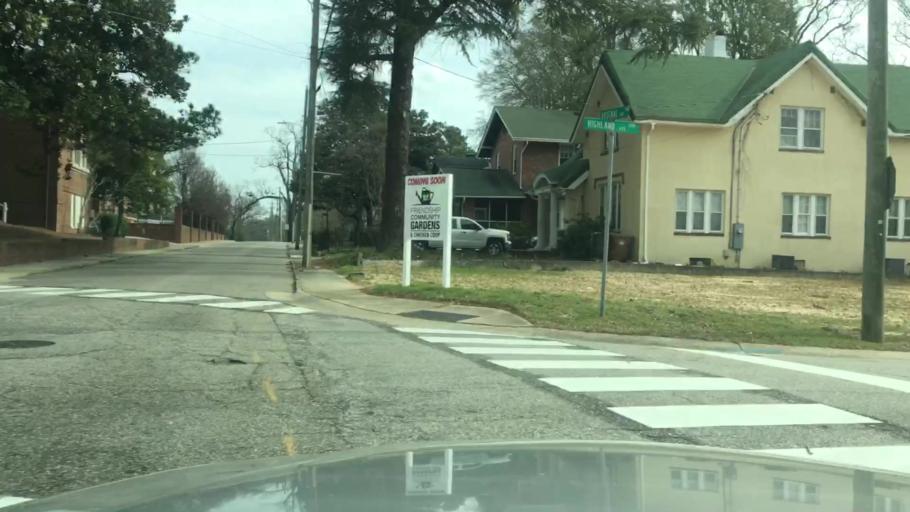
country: US
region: North Carolina
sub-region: Cumberland County
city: Fayetteville
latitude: 35.0549
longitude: -78.8993
